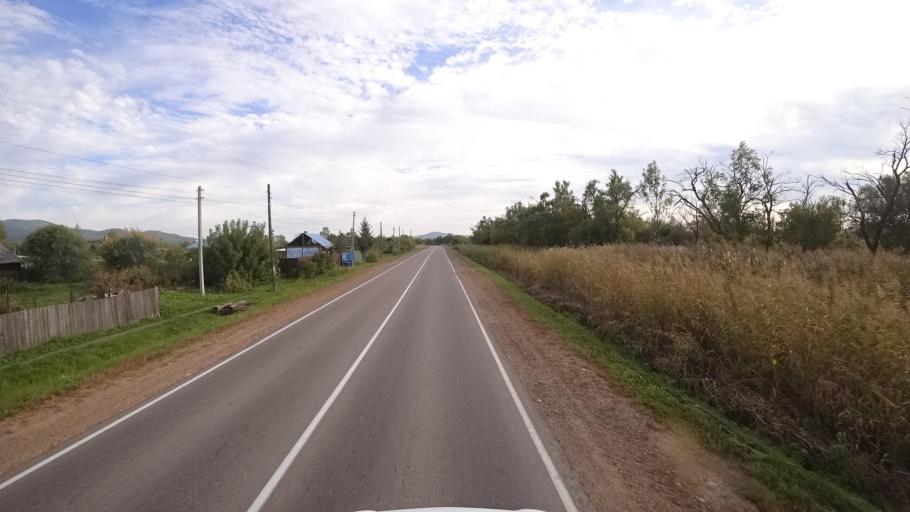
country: RU
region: Primorskiy
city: Dostoyevka
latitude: 44.2869
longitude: 133.4264
